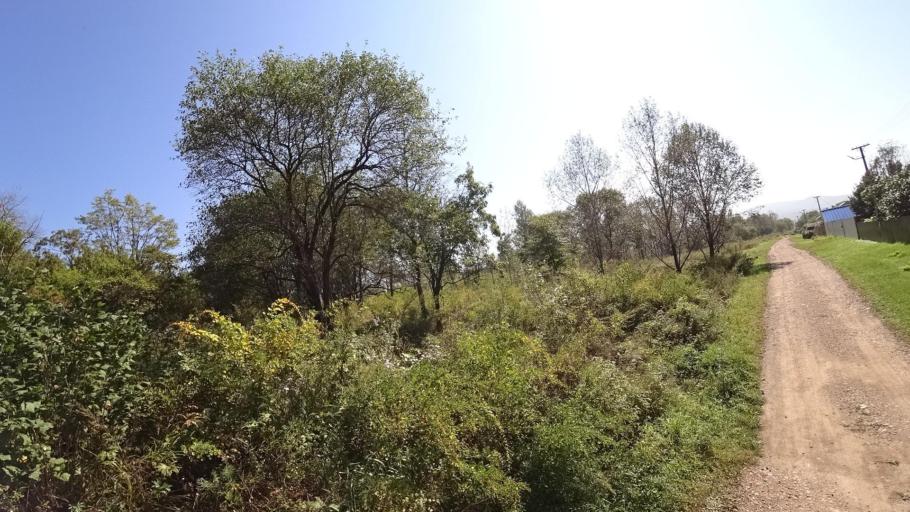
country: RU
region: Jewish Autonomous Oblast
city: Bira
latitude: 49.0136
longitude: 132.2321
